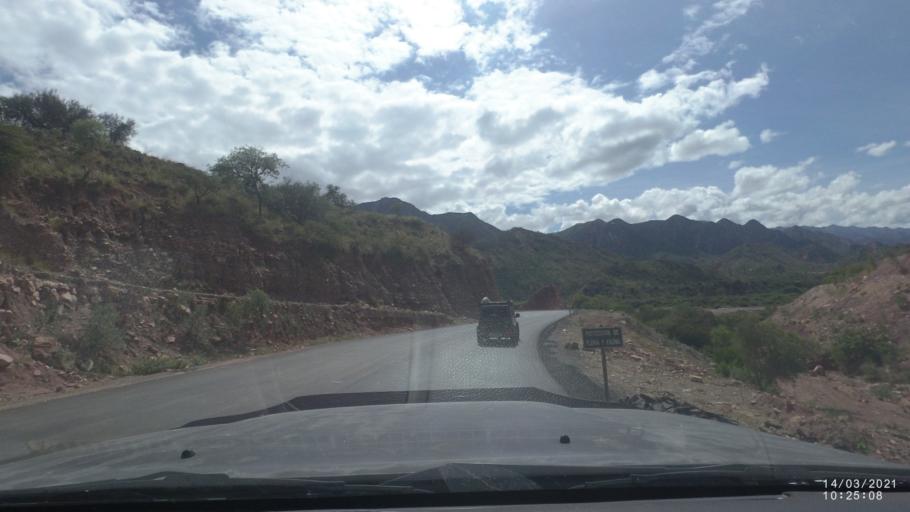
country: BO
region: Cochabamba
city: Cliza
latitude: -17.9111
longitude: -65.8801
